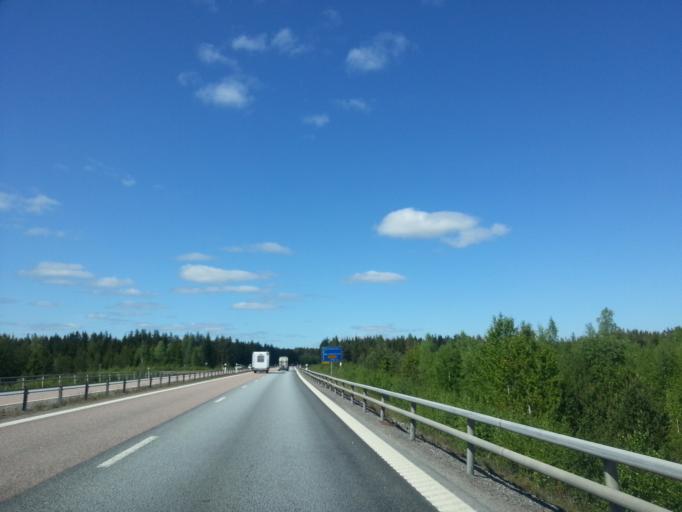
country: SE
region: Gaevleborg
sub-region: Soderhamns Kommun
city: Soderhamn
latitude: 61.4213
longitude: 16.9855
